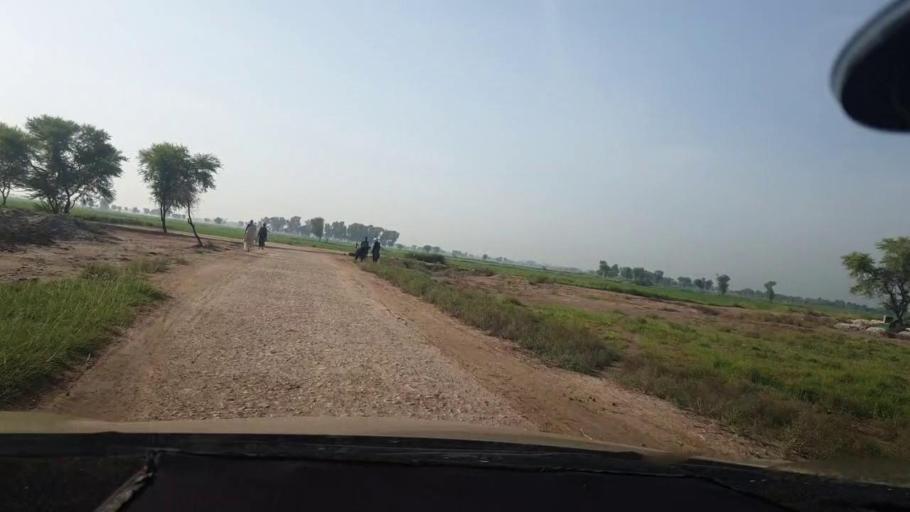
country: PK
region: Sindh
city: Kambar
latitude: 27.6418
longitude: 68.0439
